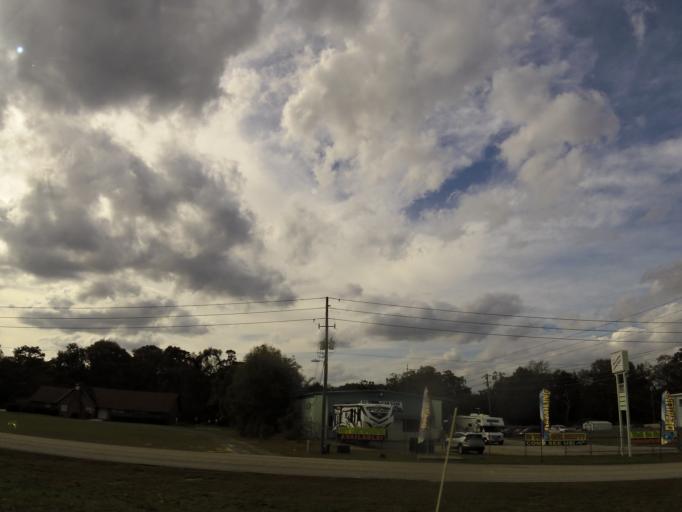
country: US
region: Florida
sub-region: Volusia County
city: Orange City
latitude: 28.9769
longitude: -81.3006
